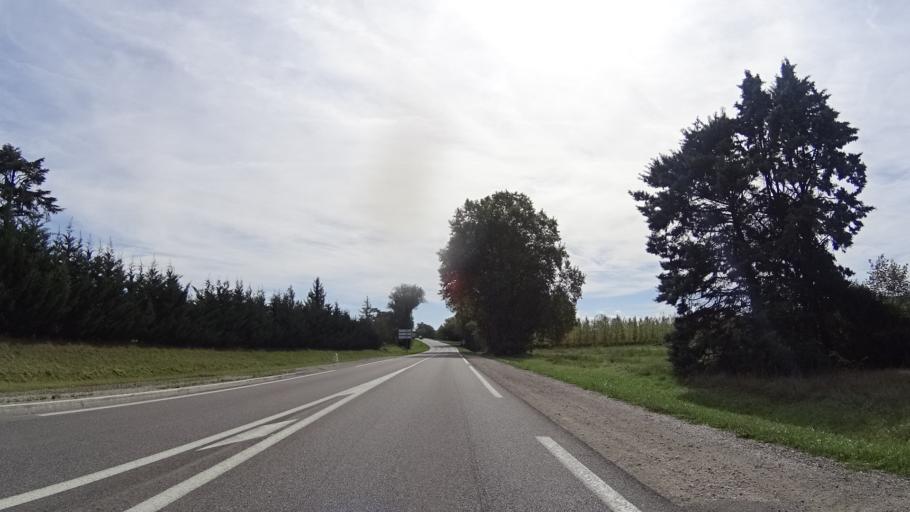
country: FR
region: Aquitaine
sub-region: Departement du Lot-et-Garonne
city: Layrac
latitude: 44.1541
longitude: 0.6545
